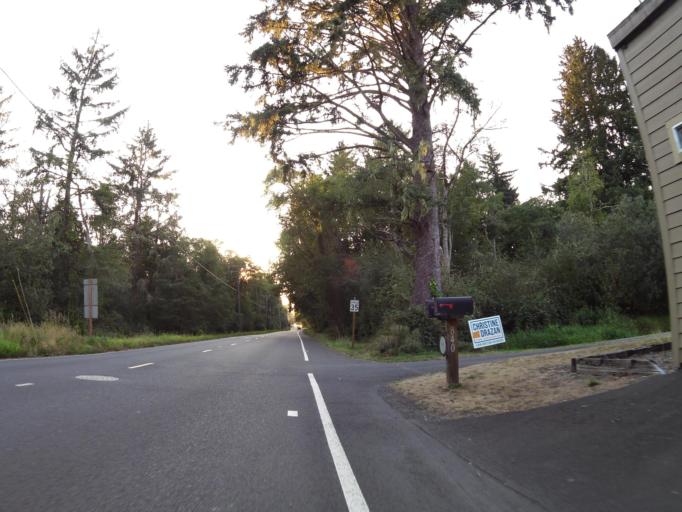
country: US
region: Oregon
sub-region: Clatsop County
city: Warrenton
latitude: 46.1577
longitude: -123.9330
